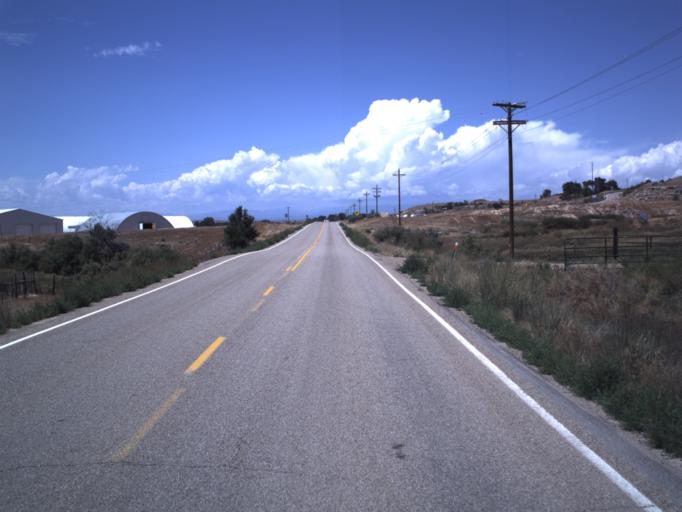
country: US
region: Utah
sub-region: Uintah County
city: Maeser
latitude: 40.2175
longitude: -109.6793
